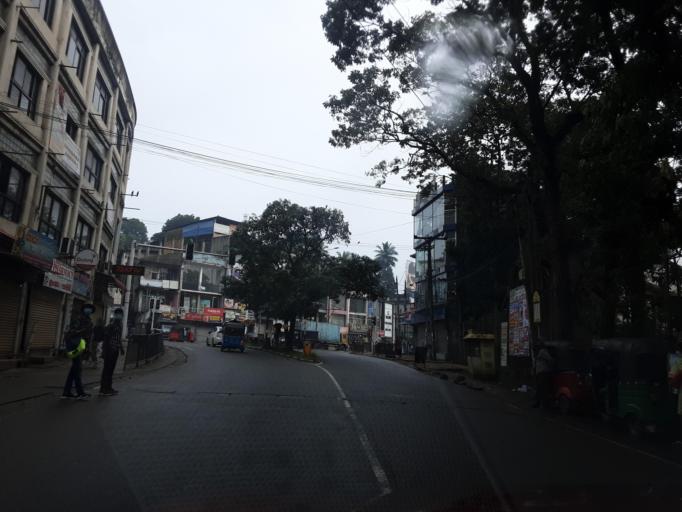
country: LK
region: Central
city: Kandy
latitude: 7.3214
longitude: 80.6246
